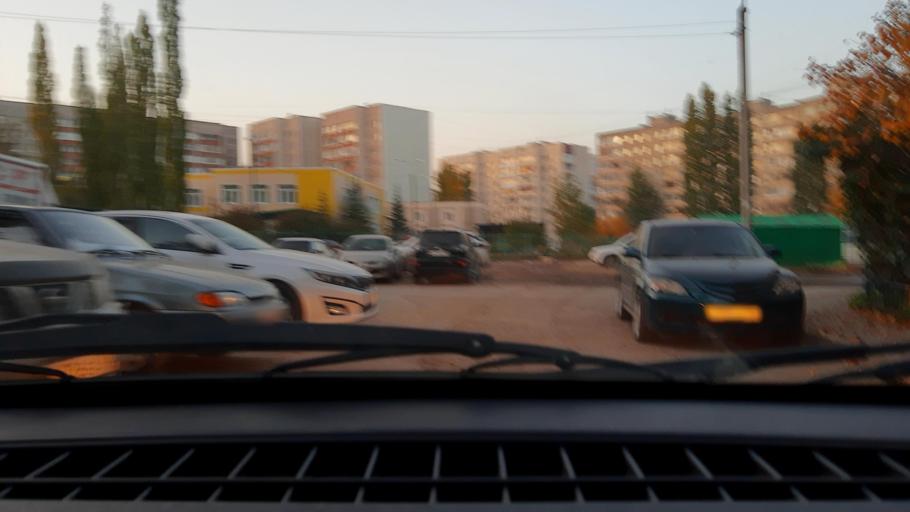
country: RU
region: Bashkortostan
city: Ufa
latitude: 54.7654
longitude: 56.0546
